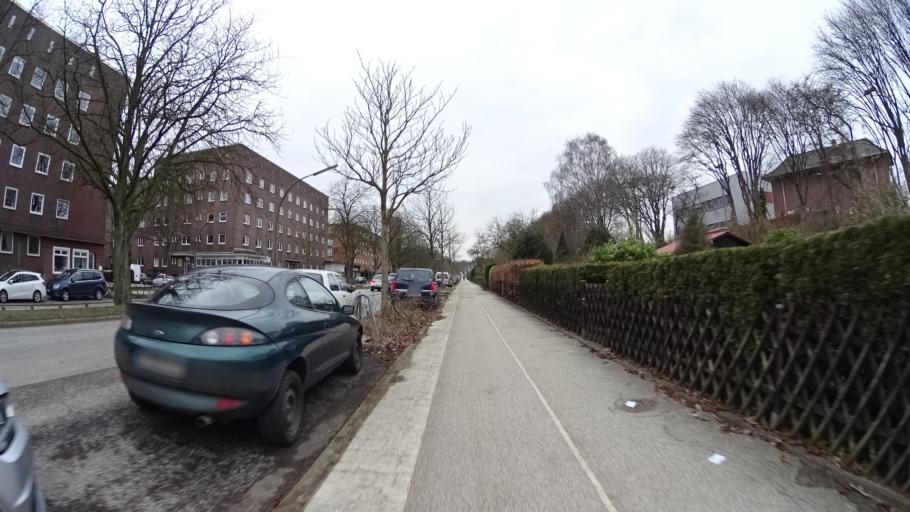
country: DE
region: Hamburg
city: Hamburg
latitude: 53.5887
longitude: 10.0267
